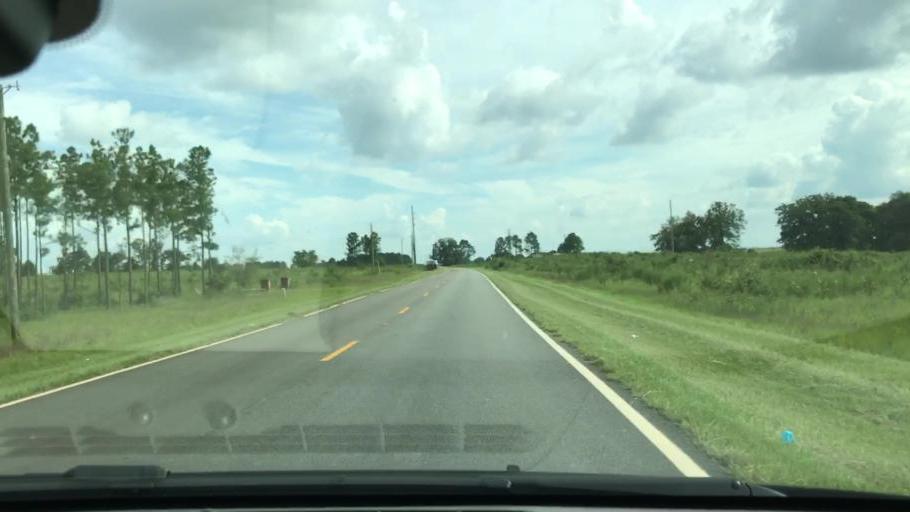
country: US
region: Georgia
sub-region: Clay County
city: Fort Gaines
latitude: 31.5418
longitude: -84.9628
